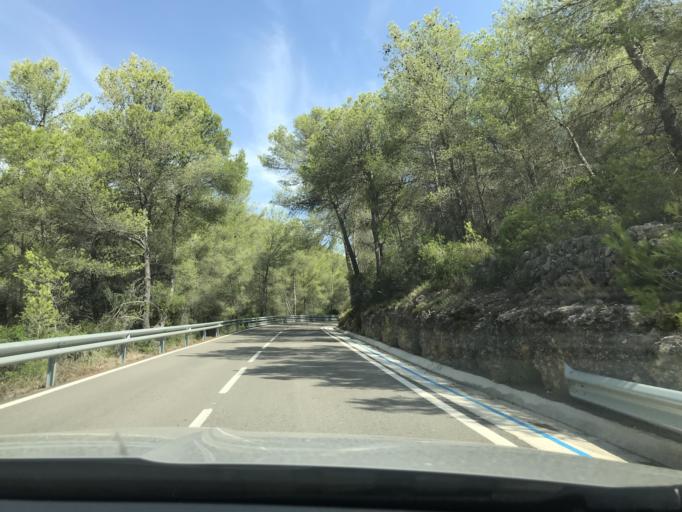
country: ES
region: Catalonia
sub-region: Provincia de Tarragona
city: Salomo
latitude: 41.1968
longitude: 1.3848
